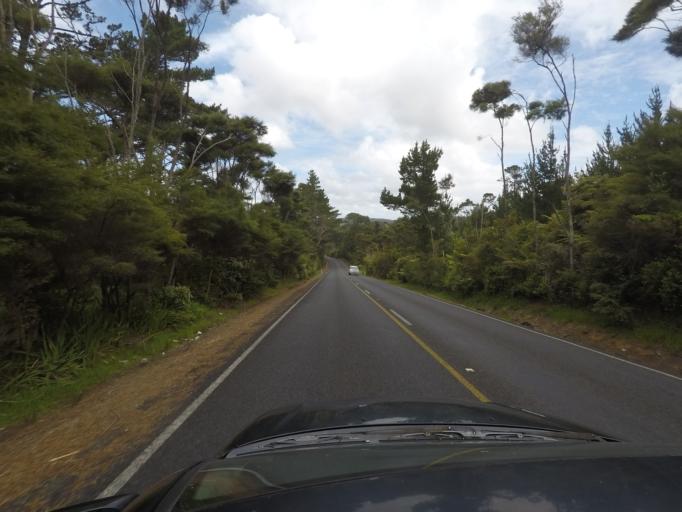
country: NZ
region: Auckland
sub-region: Auckland
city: Parakai
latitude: -36.6392
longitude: 174.5078
